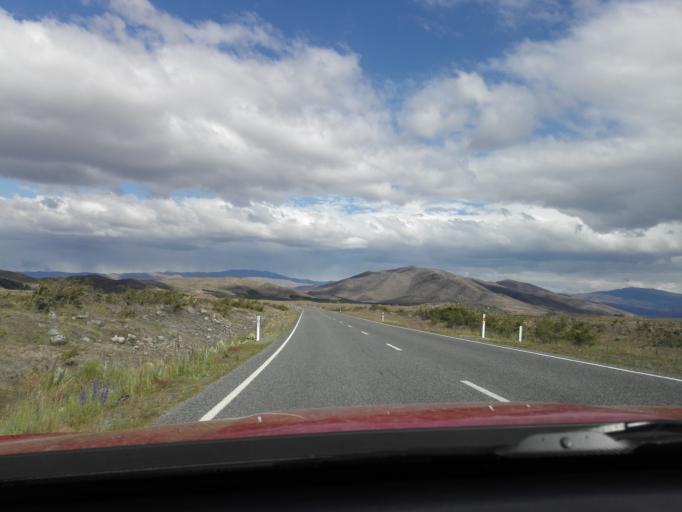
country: NZ
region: Canterbury
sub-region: Timaru District
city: Pleasant Point
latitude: -44.1998
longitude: 170.2497
